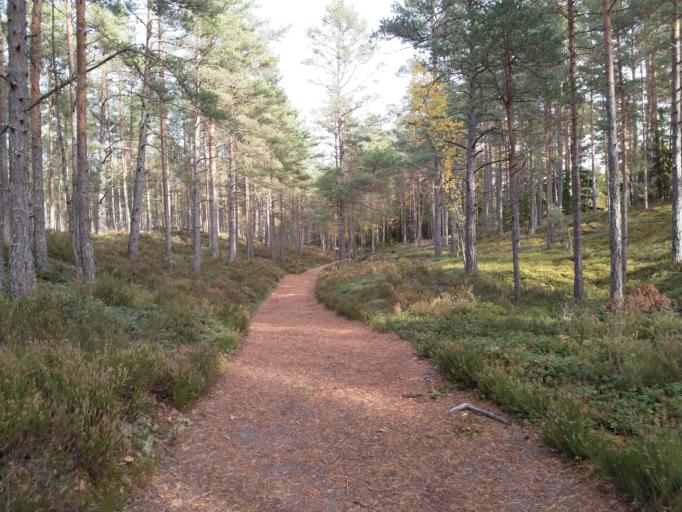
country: LV
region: Dundaga
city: Dundaga
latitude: 57.6539
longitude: 22.2661
